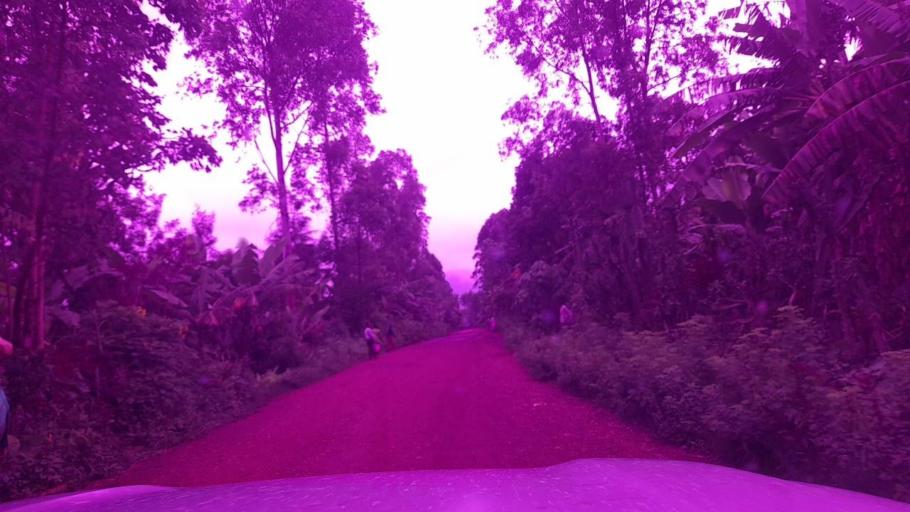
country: ET
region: Southern Nations, Nationalities, and People's Region
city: Bonga
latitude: 7.5865
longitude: 36.0157
